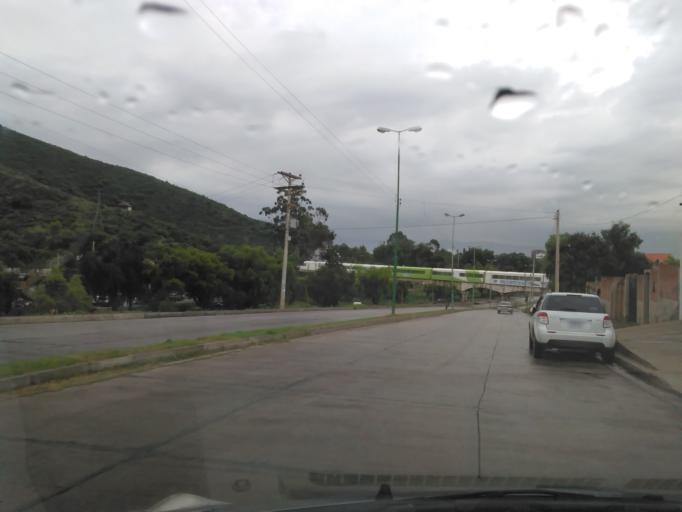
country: BO
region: Cochabamba
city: Cochabamba
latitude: -17.3746
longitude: -66.1371
